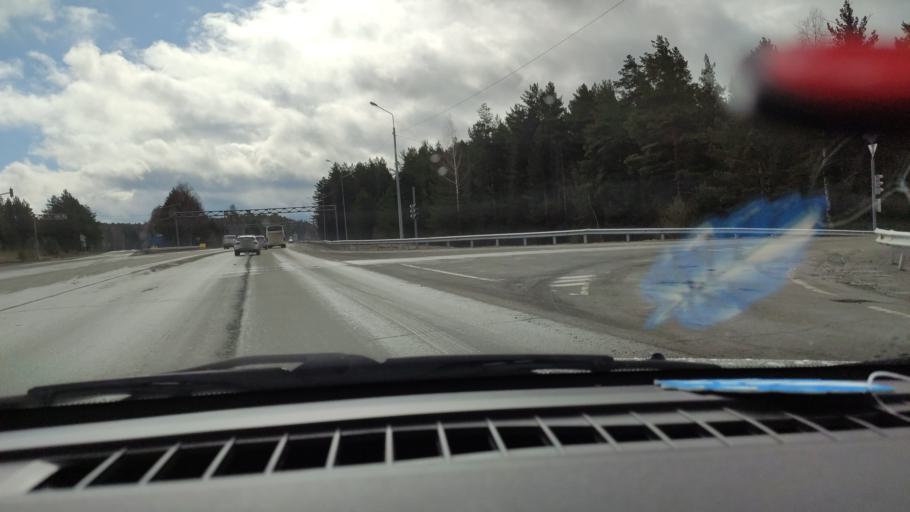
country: RU
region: Sverdlovsk
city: Talitsa
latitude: 56.8735
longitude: 60.0341
